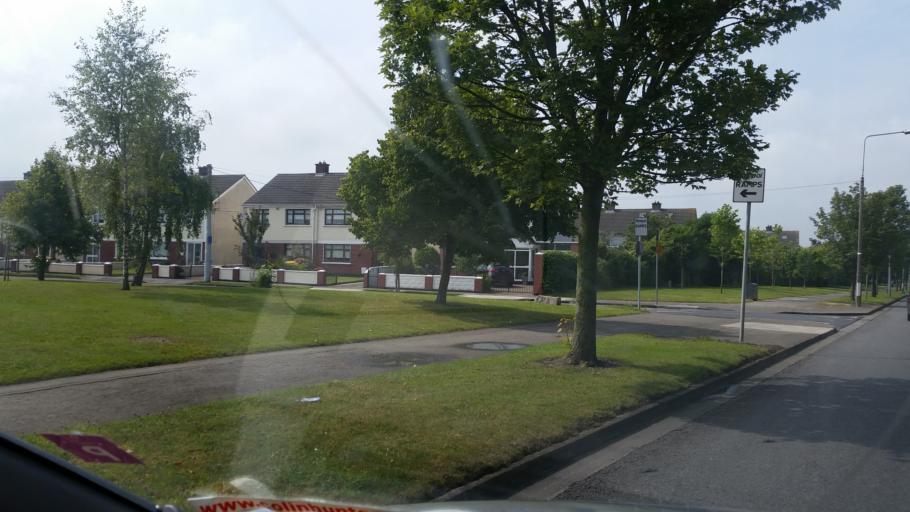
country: IE
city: Bonnybrook
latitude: 53.3925
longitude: -6.2067
